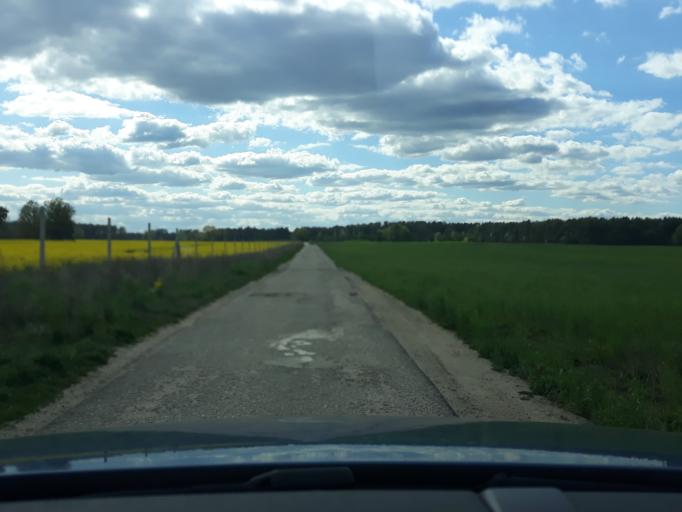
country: PL
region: Pomeranian Voivodeship
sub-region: Powiat czluchowski
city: Czluchow
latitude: 53.7193
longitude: 17.3604
